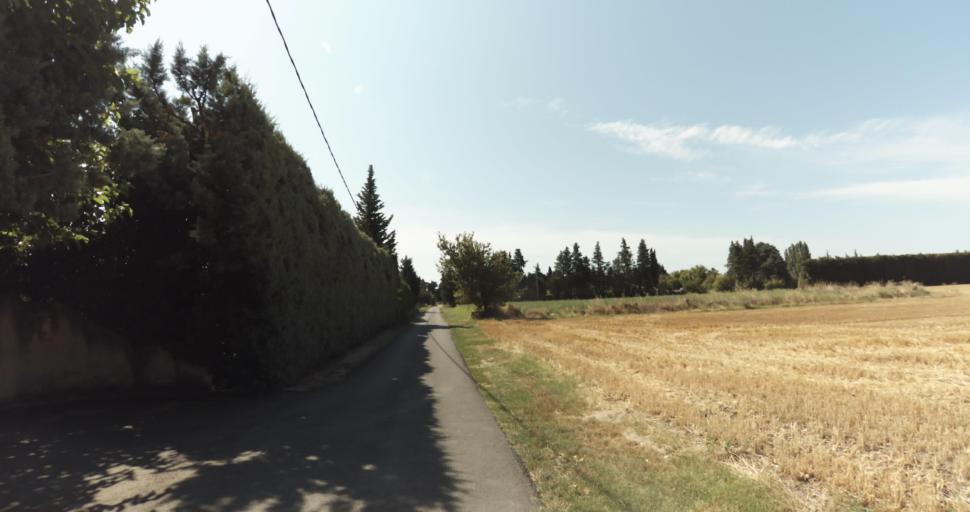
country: FR
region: Provence-Alpes-Cote d'Azur
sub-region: Departement du Vaucluse
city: Monteux
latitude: 44.0153
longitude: 5.0012
